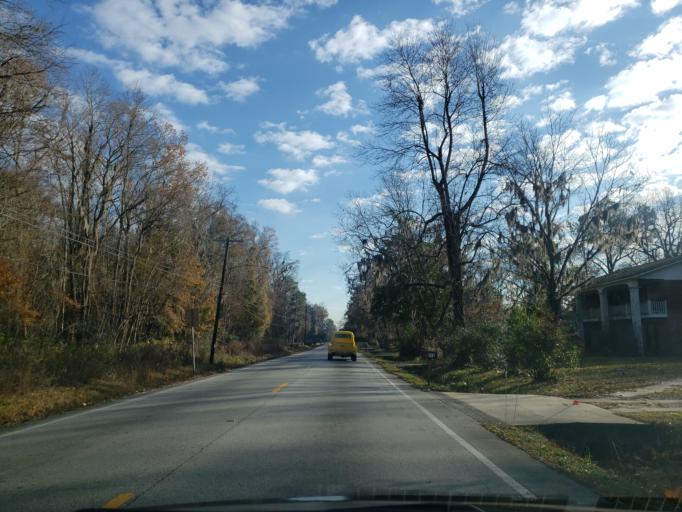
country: US
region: Georgia
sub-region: Chatham County
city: Port Wentworth
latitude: 32.1561
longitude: -81.1706
